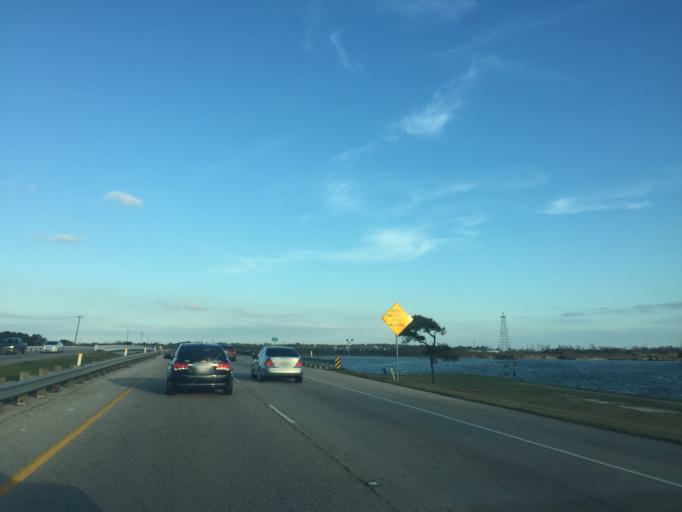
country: US
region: Texas
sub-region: Harris County
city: Baytown
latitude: 29.7137
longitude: -94.9933
